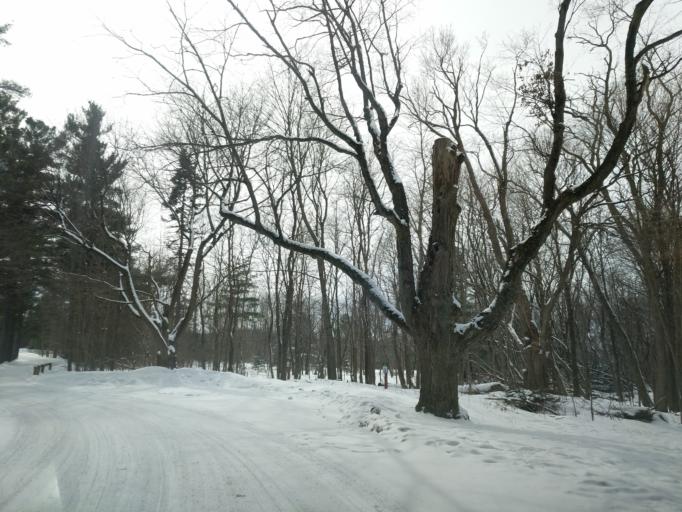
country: CA
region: Ontario
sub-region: York
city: Richmond Hill
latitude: 43.9543
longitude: -79.4232
